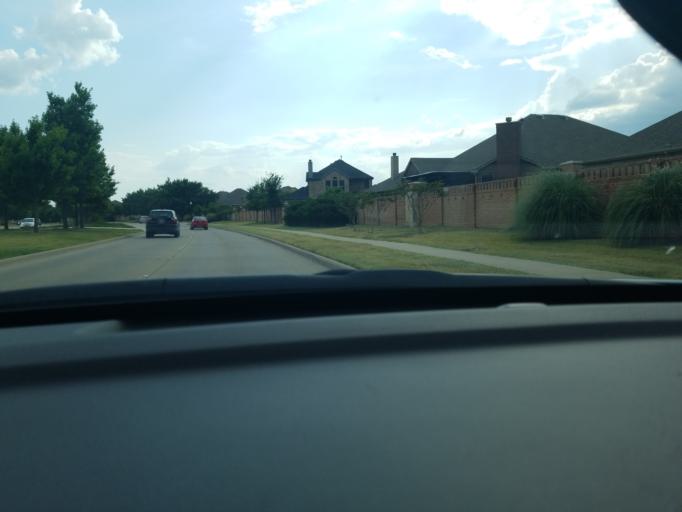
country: US
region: Texas
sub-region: Denton County
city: Little Elm
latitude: 33.1781
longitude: -96.8922
